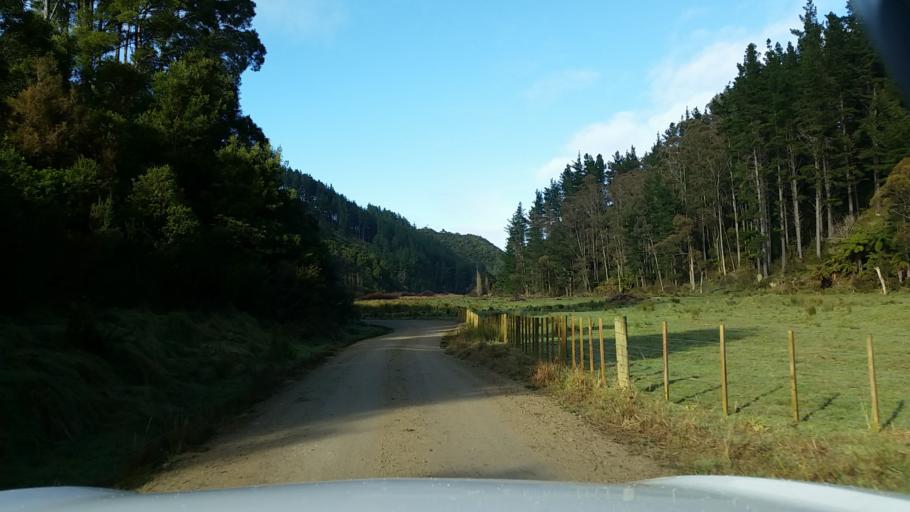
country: NZ
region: Taranaki
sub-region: South Taranaki District
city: Patea
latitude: -39.6757
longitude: 174.7645
